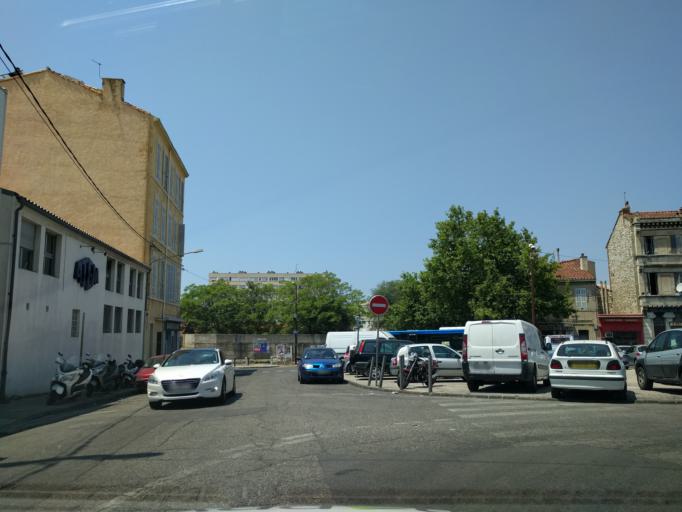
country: FR
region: Provence-Alpes-Cote d'Azur
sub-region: Departement des Bouches-du-Rhone
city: Marseille 14
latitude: 43.3370
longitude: 5.3581
